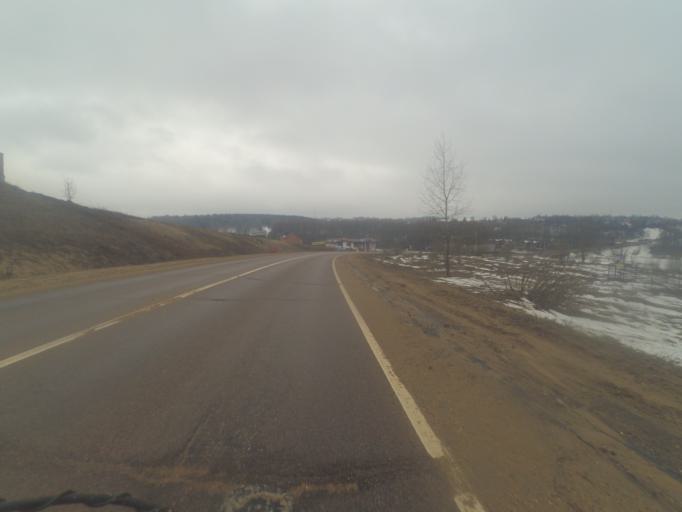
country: RU
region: Moskovskaya
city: Podosinki
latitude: 56.2719
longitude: 37.5864
